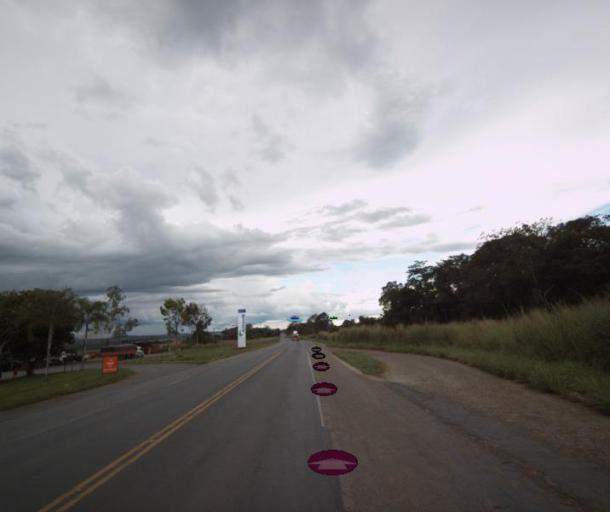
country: BR
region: Goias
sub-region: Itapaci
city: Itapaci
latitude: -15.0245
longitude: -49.4275
